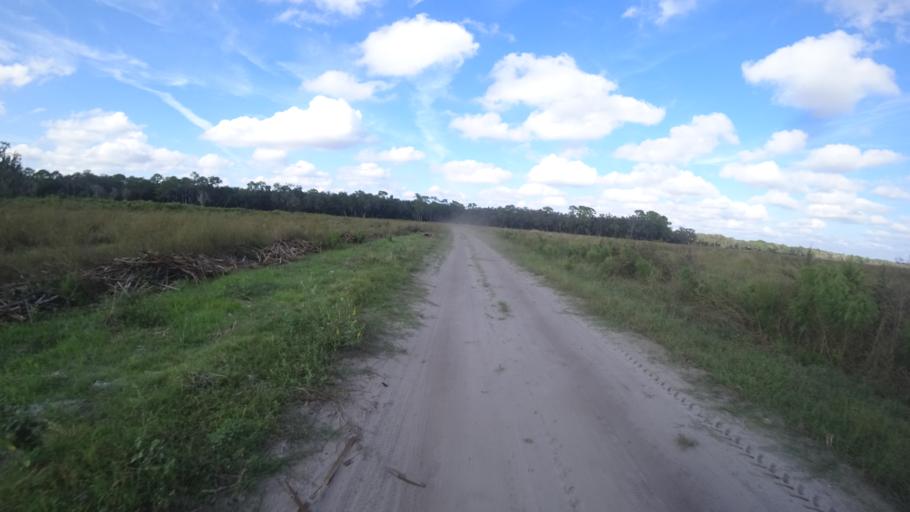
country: US
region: Florida
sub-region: DeSoto County
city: Arcadia
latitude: 27.3466
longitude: -82.1146
